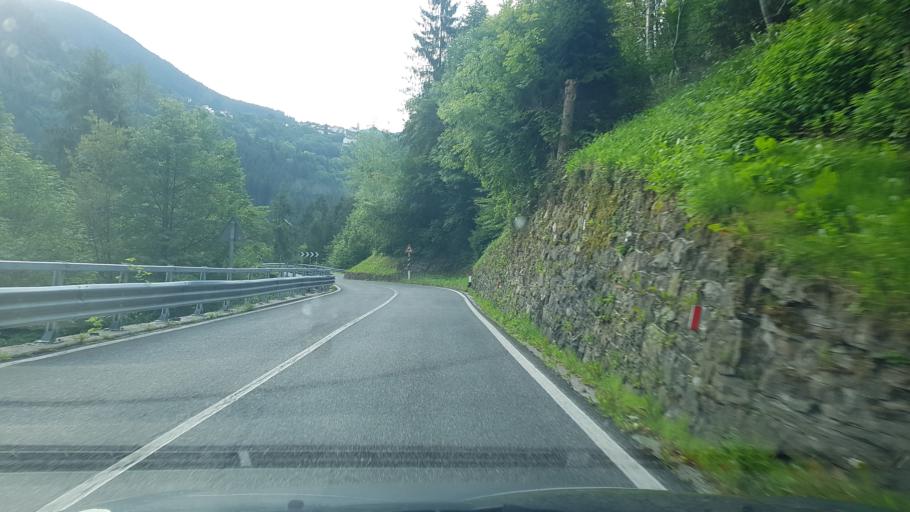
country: IT
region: Friuli Venezia Giulia
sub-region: Provincia di Udine
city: Comeglians
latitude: 46.5372
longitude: 12.8624
